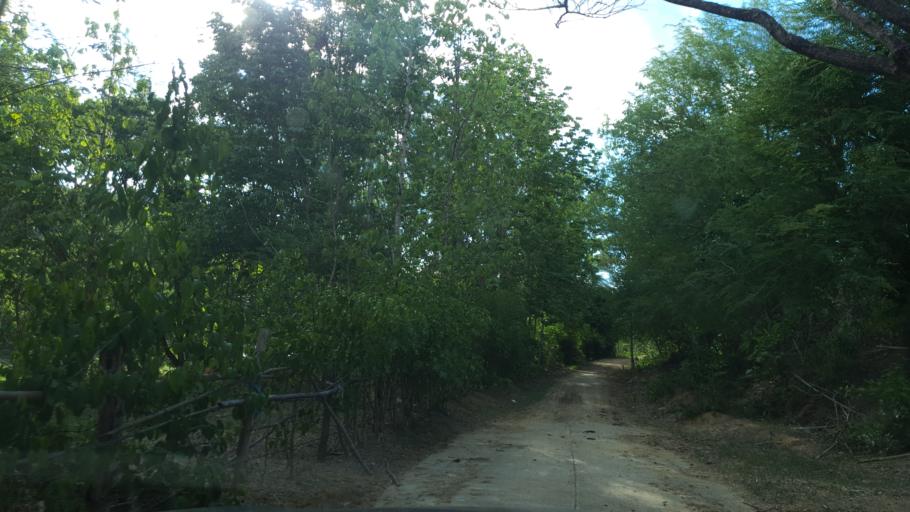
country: TH
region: Lampang
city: Sop Prap
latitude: 17.8811
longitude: 99.2947
